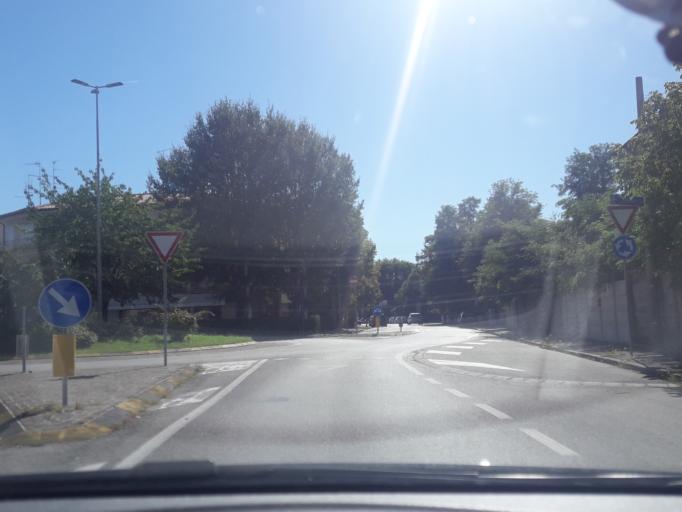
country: IT
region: Friuli Venezia Giulia
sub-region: Provincia di Udine
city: Udine
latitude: 46.0576
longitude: 13.2552
